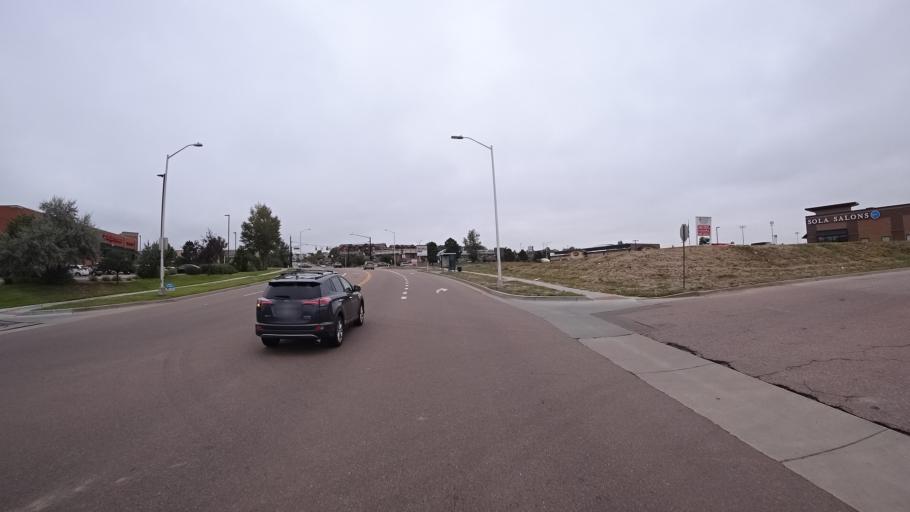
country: US
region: Colorado
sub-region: El Paso County
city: Cimarron Hills
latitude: 38.8934
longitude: -104.7140
